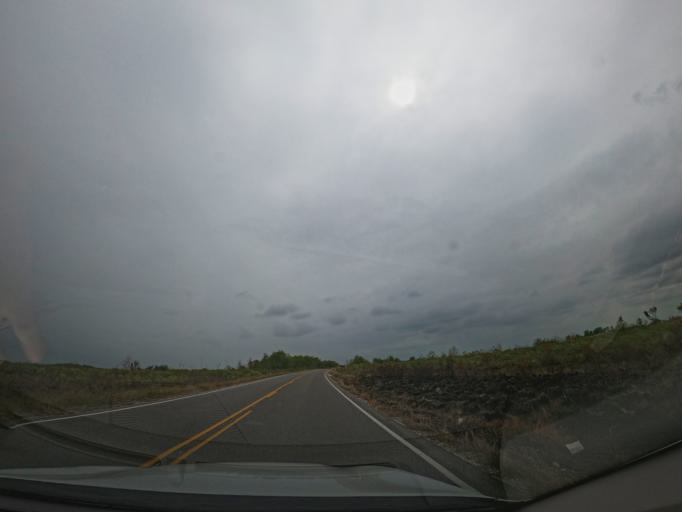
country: US
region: Louisiana
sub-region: Cameron Parish
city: Cameron
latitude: 29.7981
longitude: -93.3501
